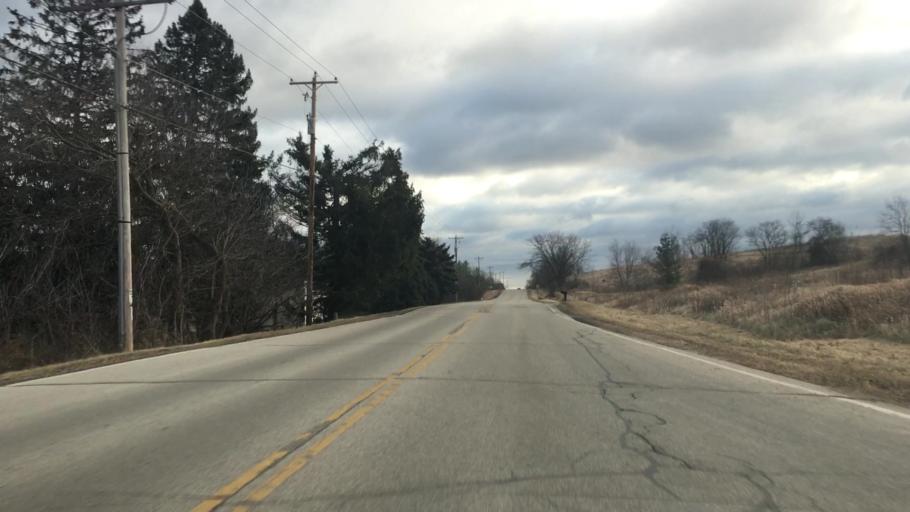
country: US
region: Wisconsin
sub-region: Washington County
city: Richfield
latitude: 43.2366
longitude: -88.2359
